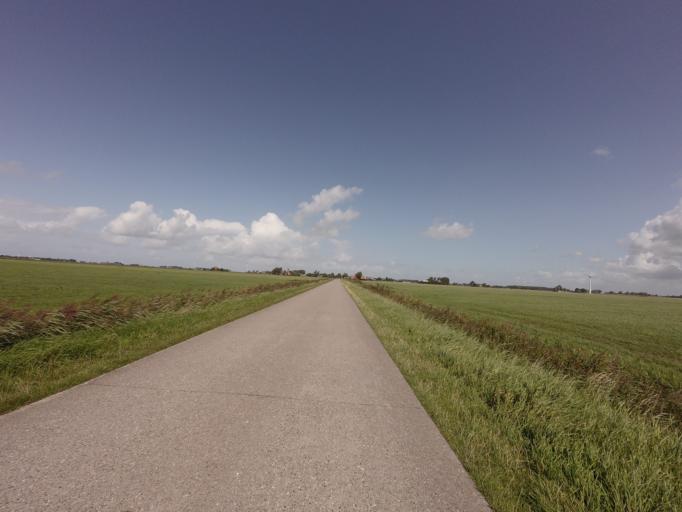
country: NL
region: Friesland
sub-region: Sudwest Fryslan
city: Makkum
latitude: 53.0714
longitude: 5.4540
